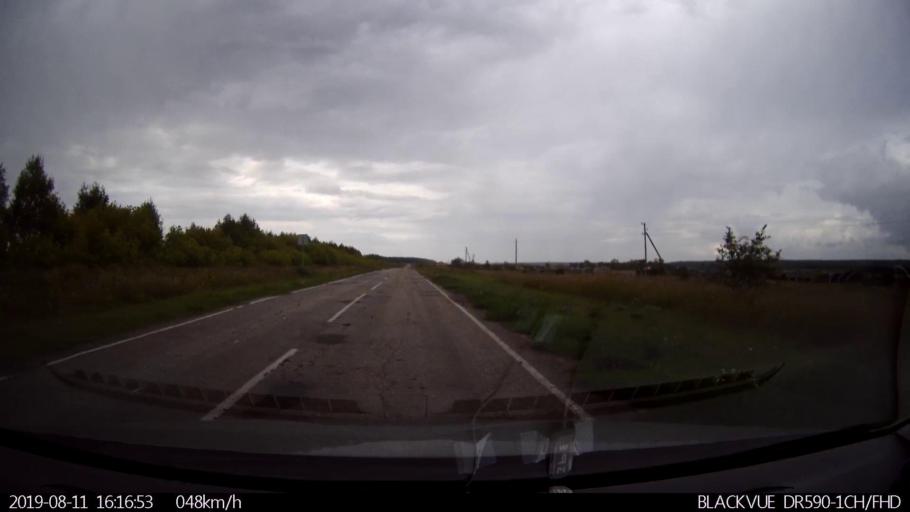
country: RU
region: Ulyanovsk
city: Mayna
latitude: 54.0444
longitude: 47.6191
